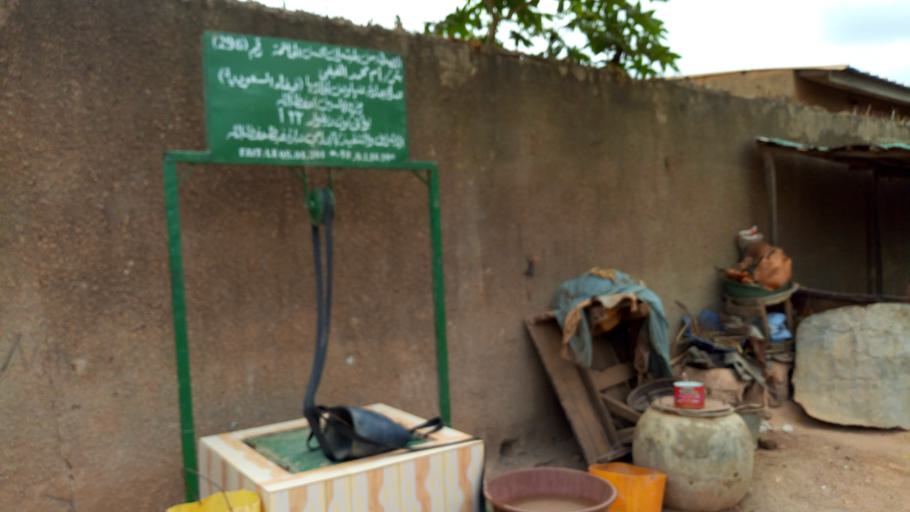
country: CI
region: Vallee du Bandama
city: Bouake
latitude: 7.7062
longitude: -5.0260
